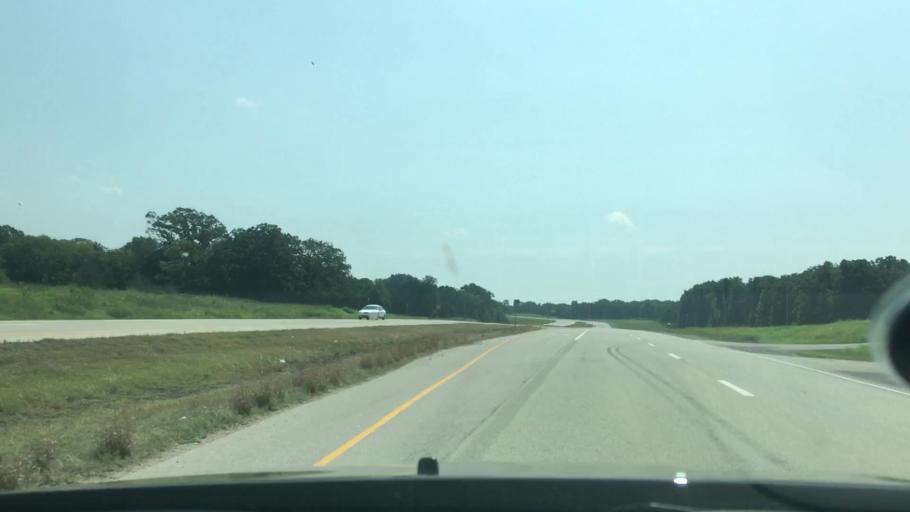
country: US
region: Oklahoma
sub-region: Atoka County
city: Atoka
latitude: 34.3208
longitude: -96.0372
